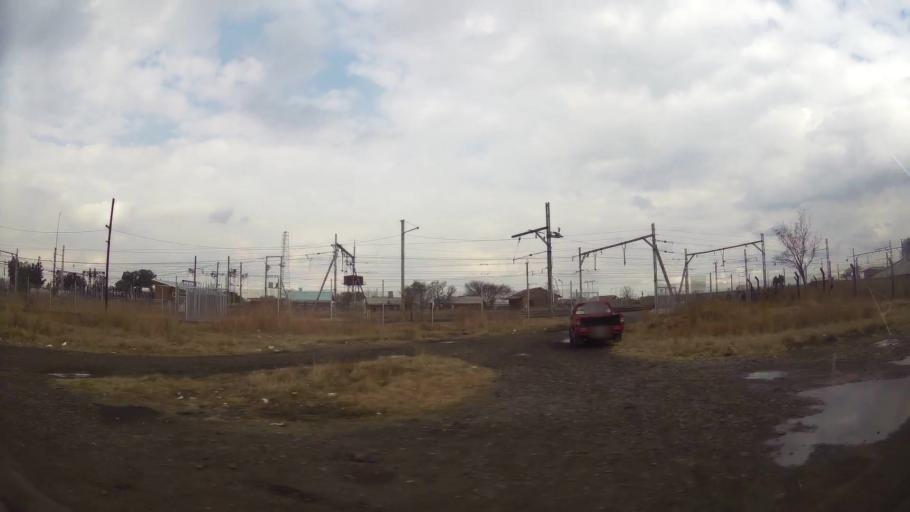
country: ZA
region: Orange Free State
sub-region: Fezile Dabi District Municipality
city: Sasolburg
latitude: -26.8459
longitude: 27.8707
